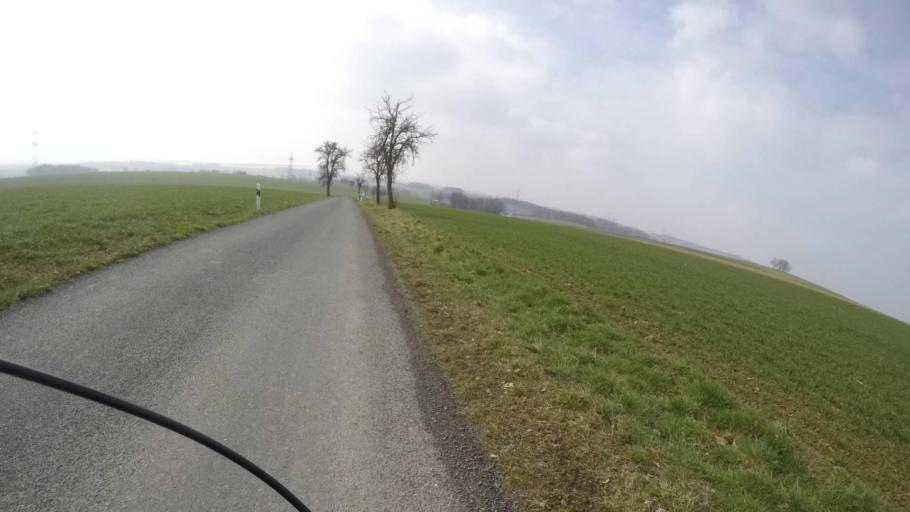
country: DE
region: Saxony
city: Niederfrohna
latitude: 50.8817
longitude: 12.6992
